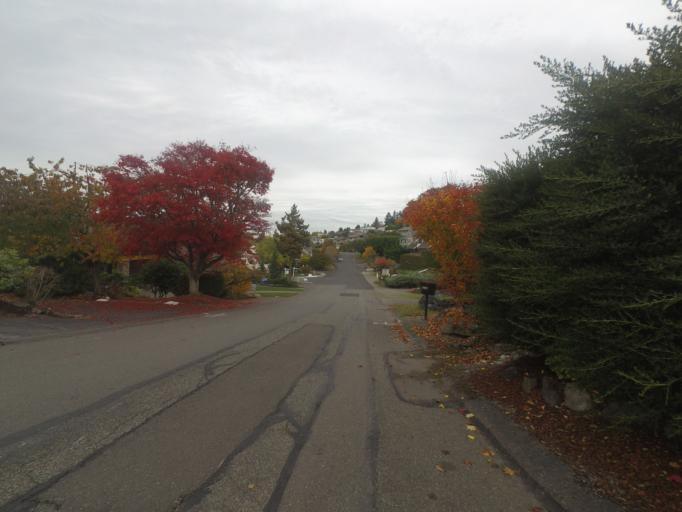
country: US
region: Washington
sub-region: Pierce County
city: University Place
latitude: 47.2246
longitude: -122.5633
